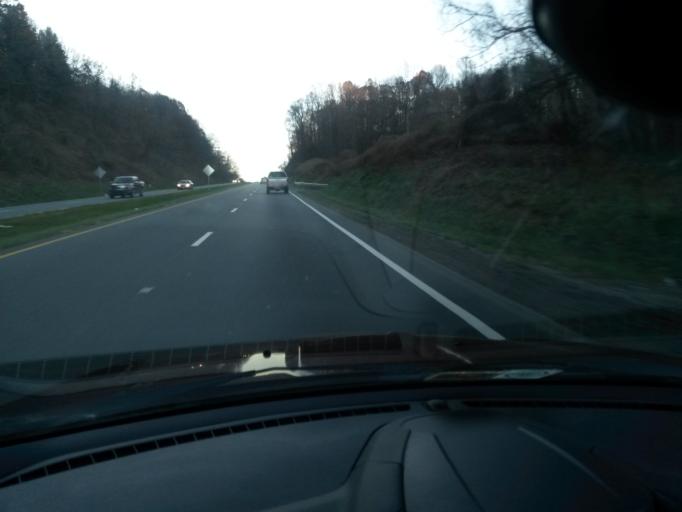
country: US
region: Virginia
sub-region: Roanoke County
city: Narrows
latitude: 37.1008
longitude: -79.9415
